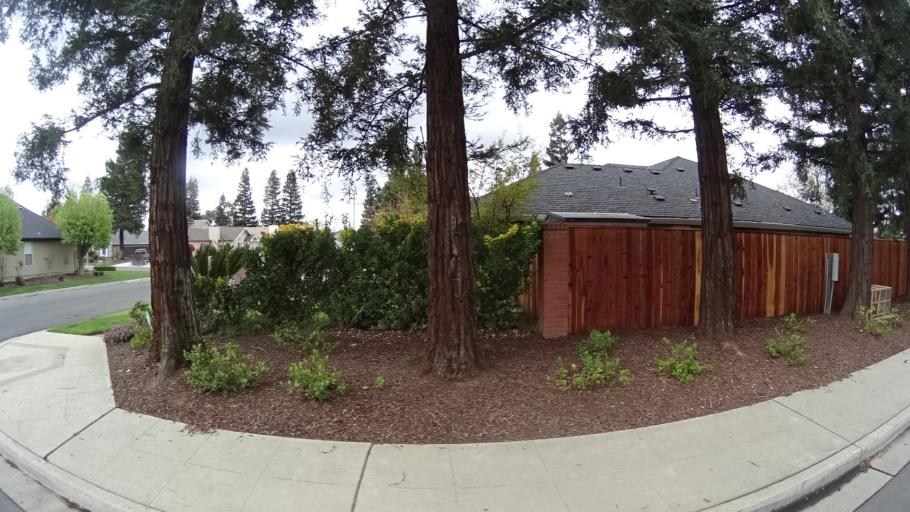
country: US
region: California
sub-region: Fresno County
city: Fresno
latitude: 36.8406
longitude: -119.8260
